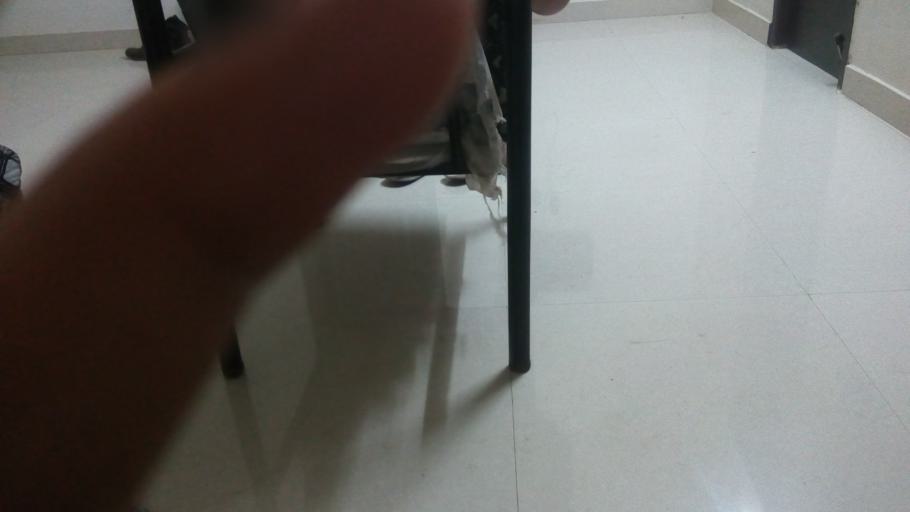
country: IN
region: Tamil Nadu
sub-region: Kancheepuram
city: Perungudi
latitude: 12.9472
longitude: 80.2334
